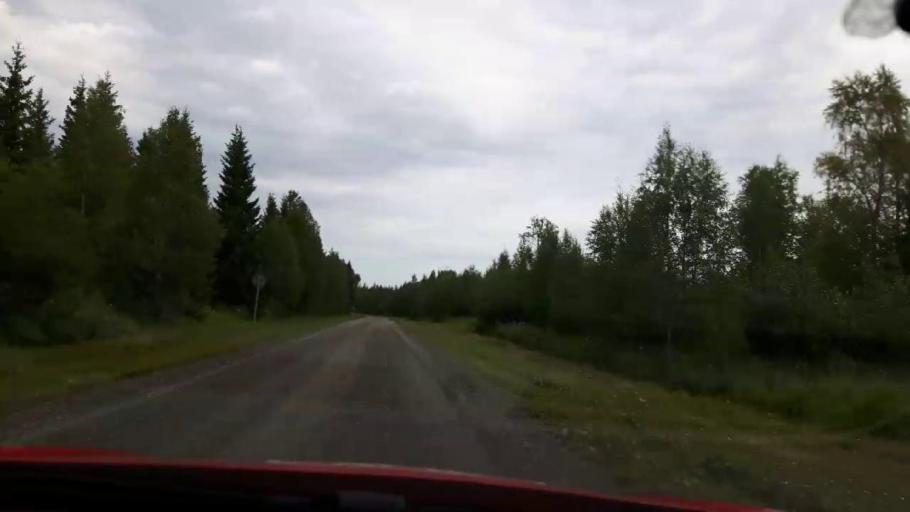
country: SE
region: Jaemtland
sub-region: Stroemsunds Kommun
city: Stroemsund
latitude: 63.7514
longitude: 15.5940
